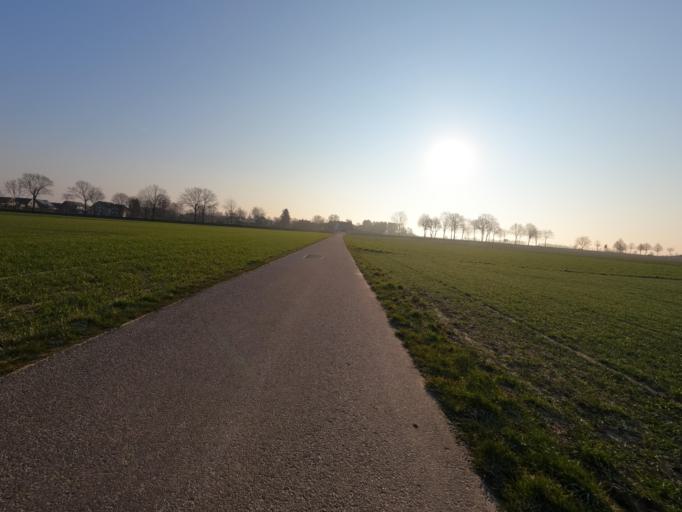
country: DE
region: North Rhine-Westphalia
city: Erkelenz
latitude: 51.0783
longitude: 6.2763
